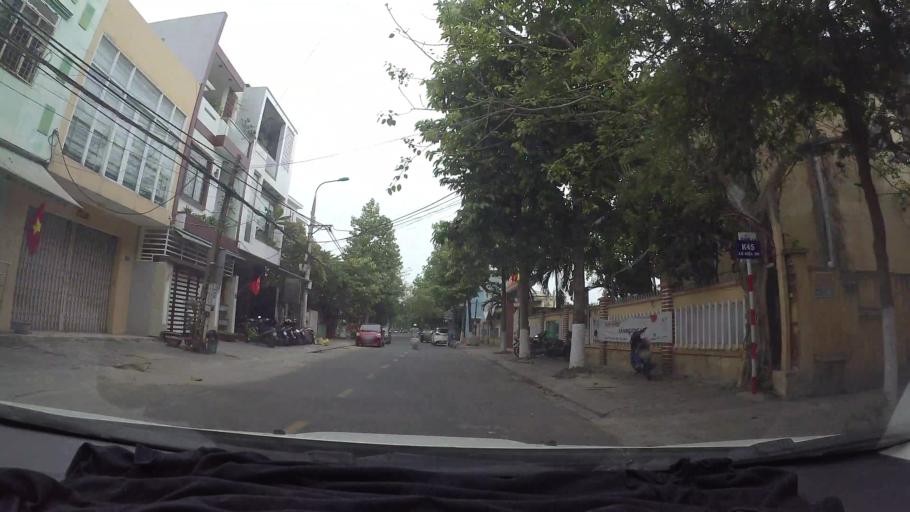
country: VN
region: Da Nang
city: Cam Le
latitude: 16.0267
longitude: 108.2097
